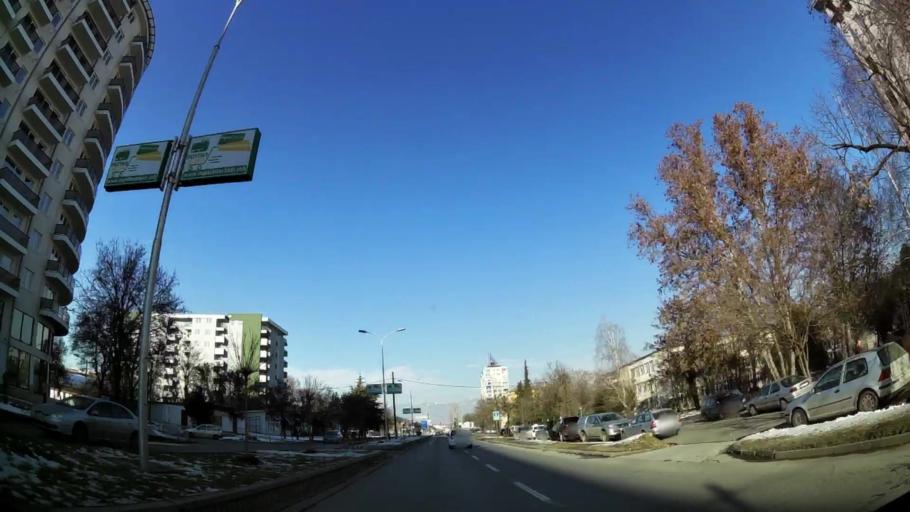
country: MK
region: Karpos
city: Skopje
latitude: 41.9996
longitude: 21.4042
